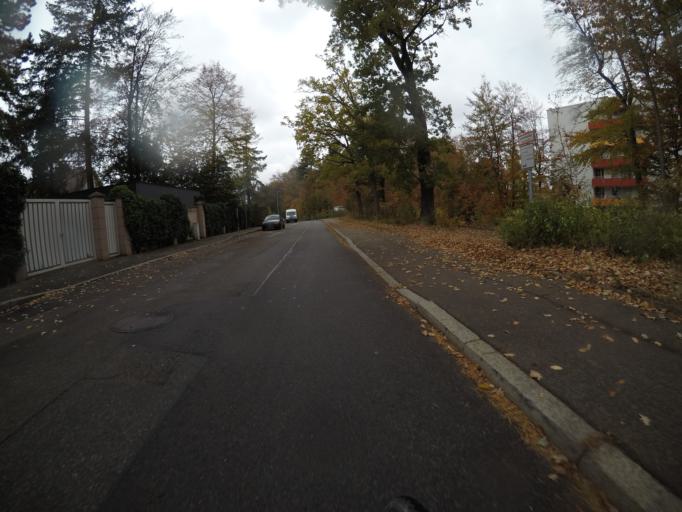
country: DE
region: Baden-Wuerttemberg
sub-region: Regierungsbezirk Stuttgart
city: Sindelfingen
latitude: 48.6891
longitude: 9.0308
